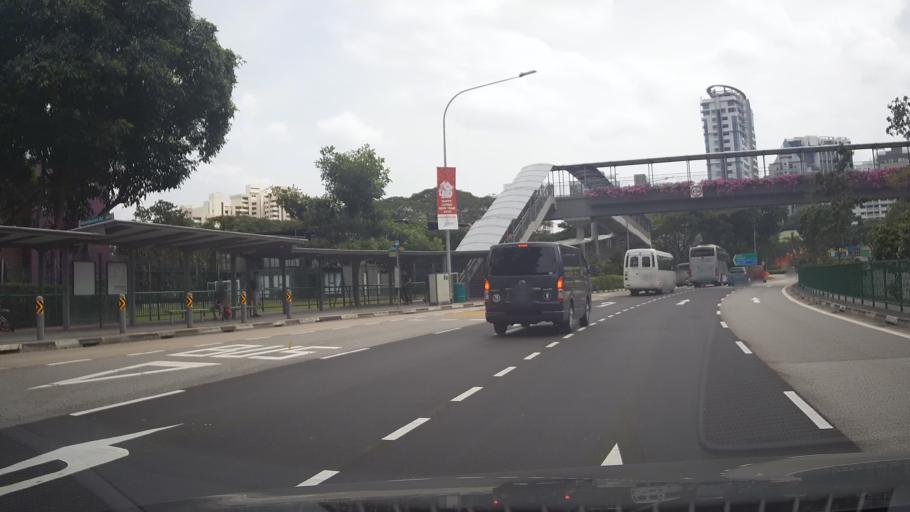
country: SG
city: Singapore
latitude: 1.3017
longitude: 103.8858
